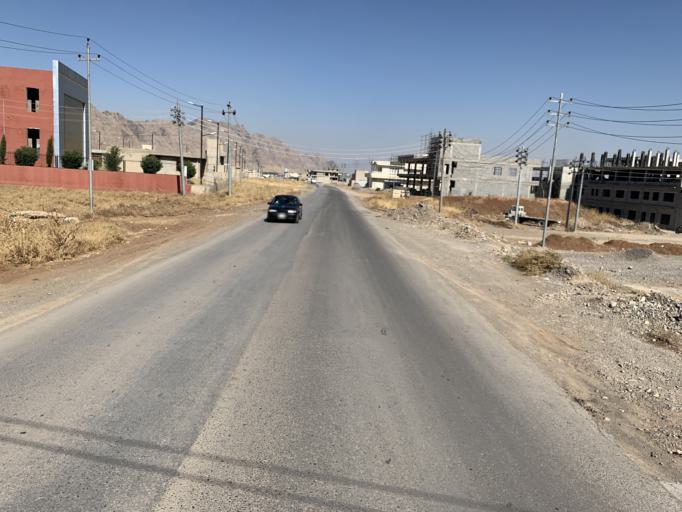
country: IQ
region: As Sulaymaniyah
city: Raniye
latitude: 36.2612
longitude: 44.8552
